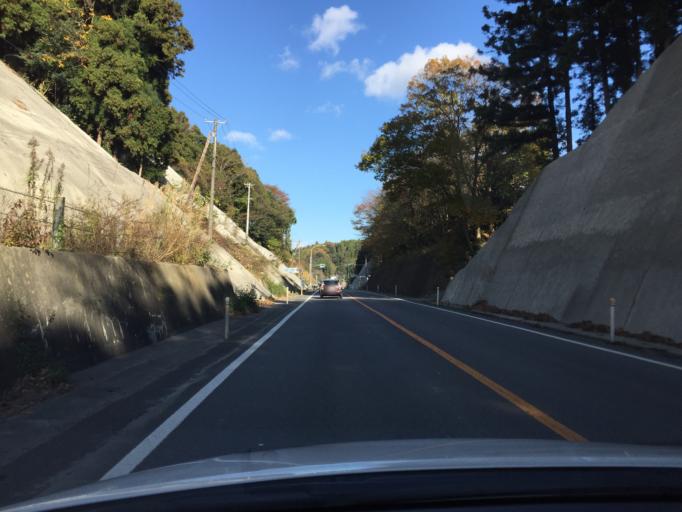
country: JP
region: Fukushima
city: Iwaki
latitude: 37.1718
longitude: 140.9938
